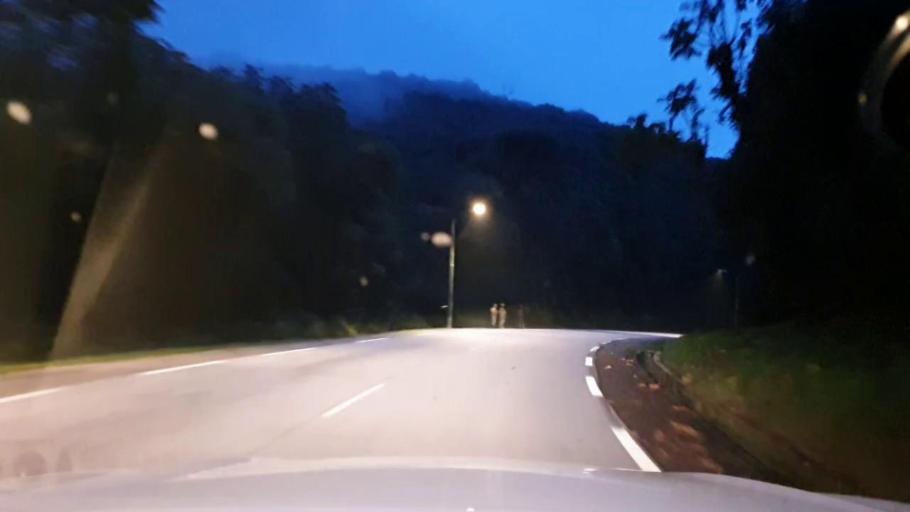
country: RW
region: Southern Province
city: Nzega
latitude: -2.5299
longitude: 29.3938
